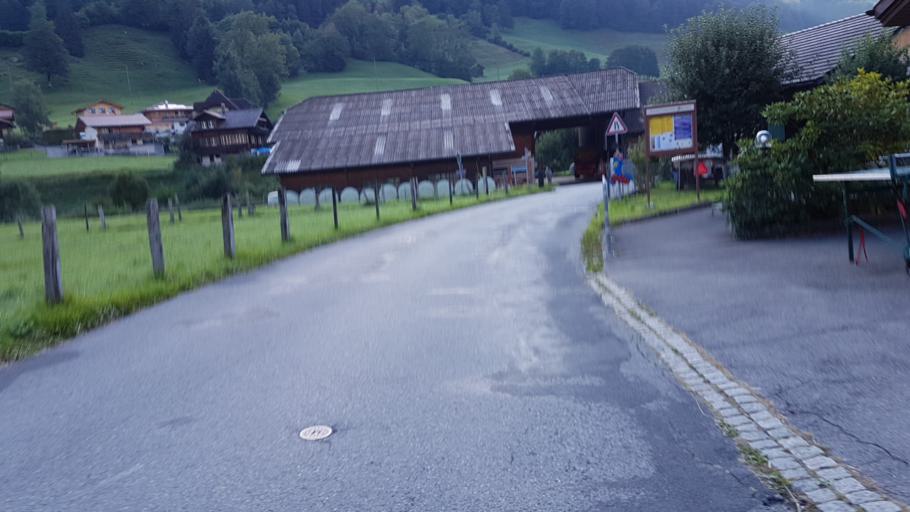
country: CH
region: Bern
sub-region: Frutigen-Niedersimmental District
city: Frutigen
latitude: 46.5834
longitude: 7.6566
